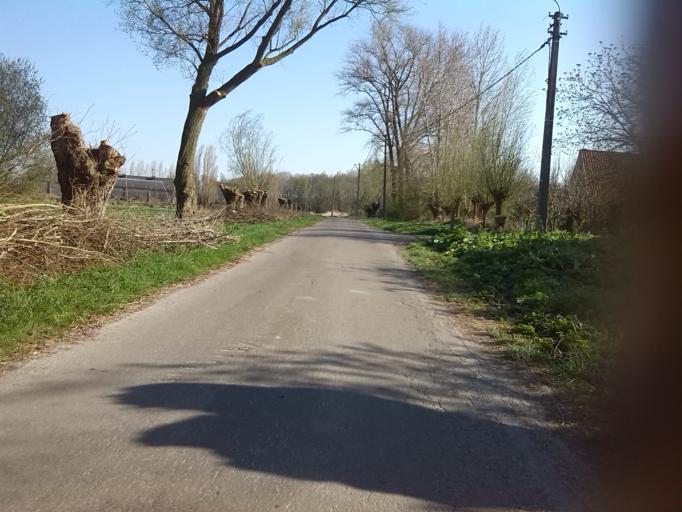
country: BE
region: Flanders
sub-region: Provincie West-Vlaanderen
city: Jabbeke
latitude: 51.2132
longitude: 3.1290
